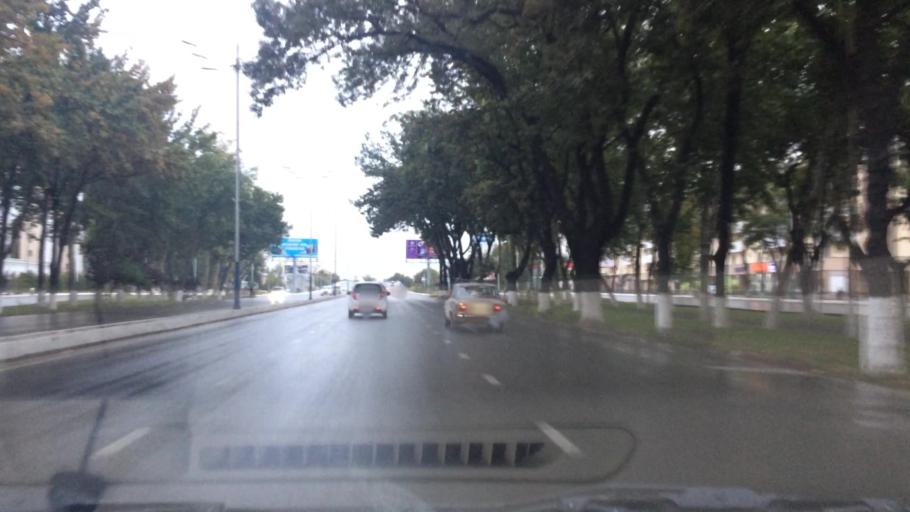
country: UZ
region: Toshkent Shahri
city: Tashkent
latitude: 41.2955
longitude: 69.2272
